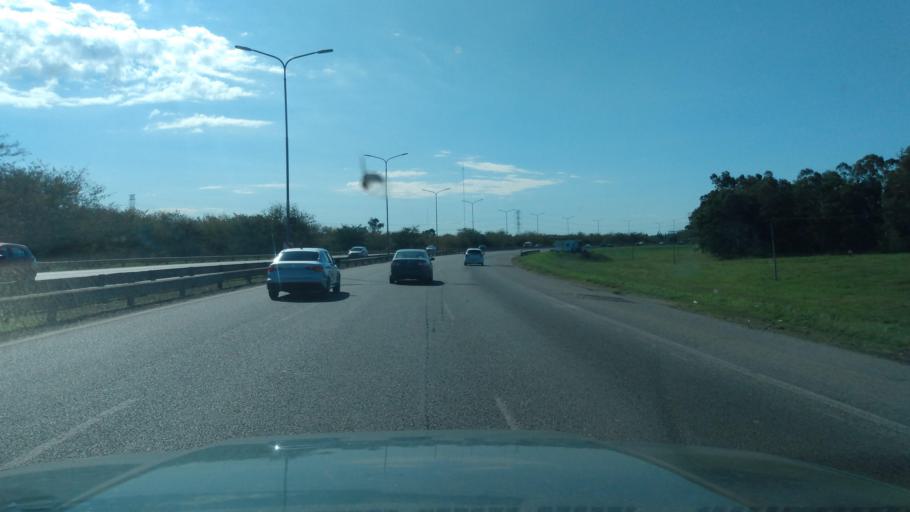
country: AR
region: Buenos Aires
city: Hurlingham
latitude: -34.5544
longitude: -58.6267
